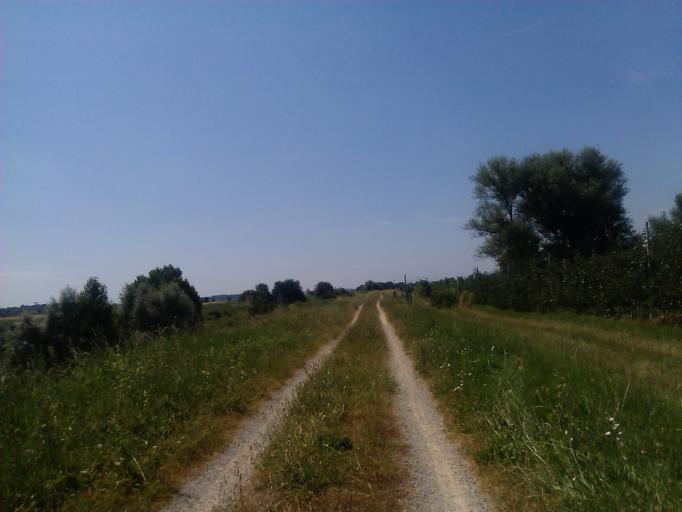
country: IT
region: Tuscany
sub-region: Province of Arezzo
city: Pieve al Toppo
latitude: 43.3713
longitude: 11.8253
